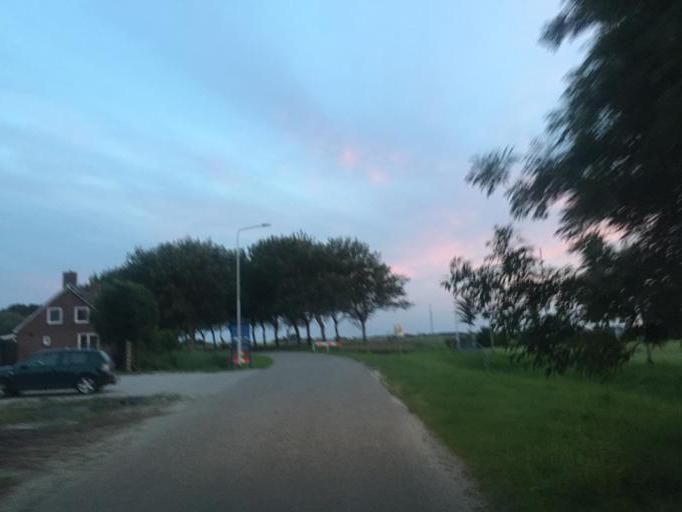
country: NL
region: Friesland
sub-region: Gemeente Dongeradeel
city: Anjum
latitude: 53.4007
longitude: 6.0862
